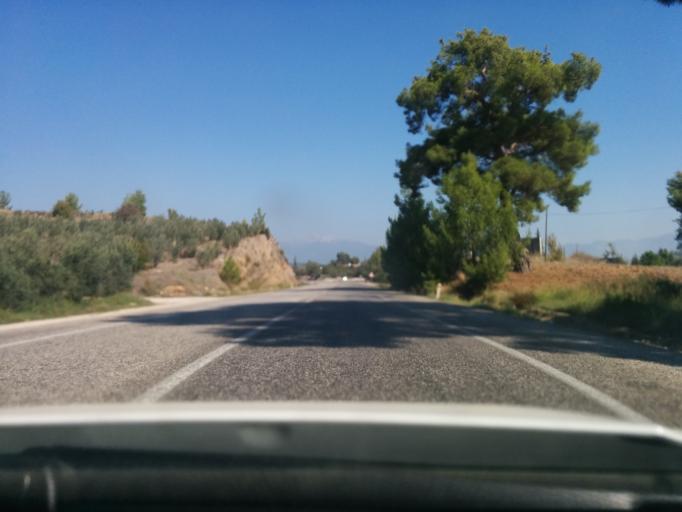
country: TR
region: Mugla
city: Kemer
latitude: 36.5584
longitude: 29.3478
